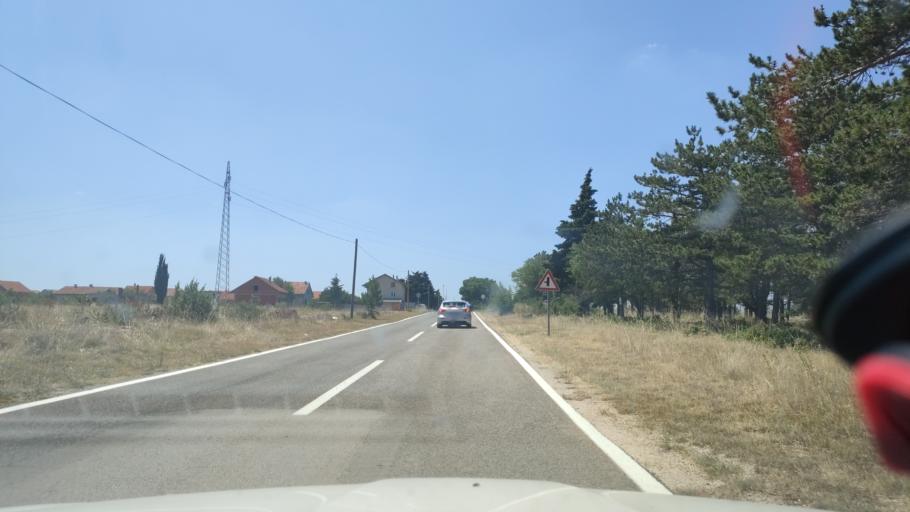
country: HR
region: Sibensko-Kniniska
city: Kistanje
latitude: 43.9868
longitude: 15.9741
